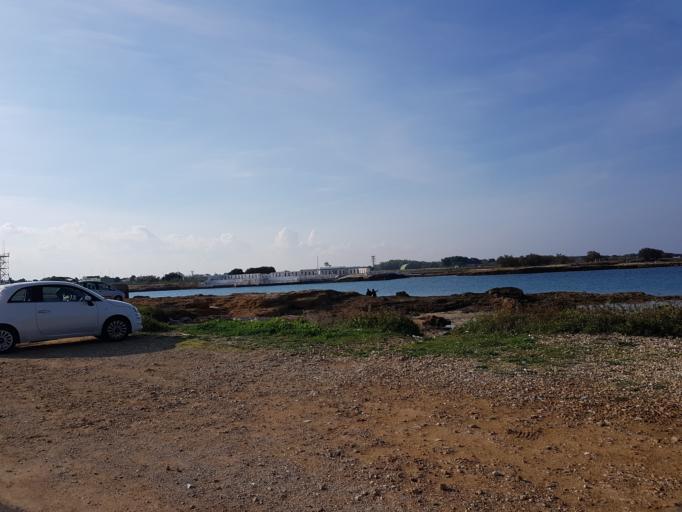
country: IT
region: Apulia
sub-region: Provincia di Brindisi
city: Materdomini
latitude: 40.6617
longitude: 17.9604
